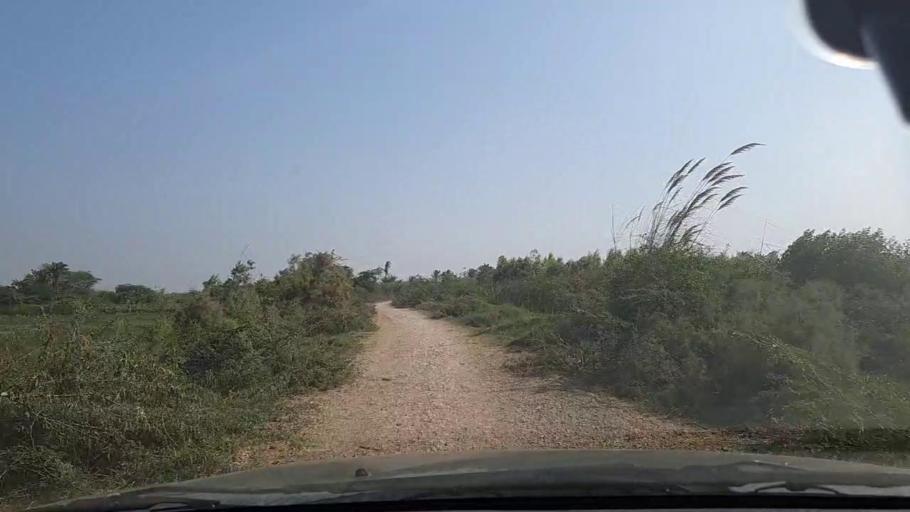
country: PK
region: Sindh
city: Chuhar Jamali
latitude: 24.5176
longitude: 67.8845
